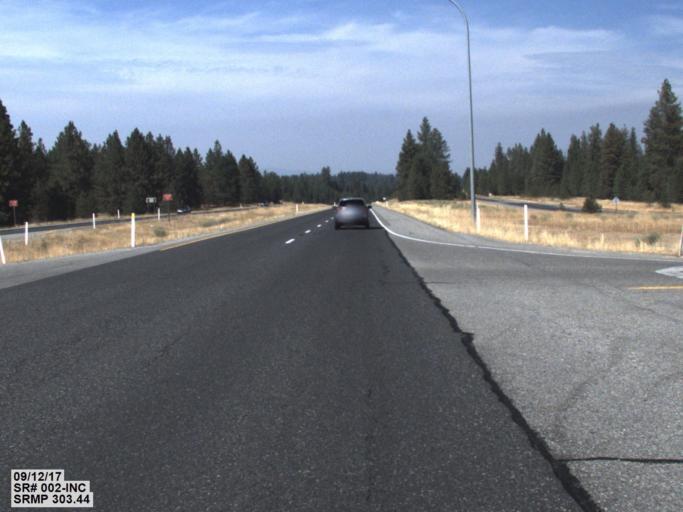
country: US
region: Washington
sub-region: Spokane County
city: Mead
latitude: 47.8748
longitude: -117.3571
